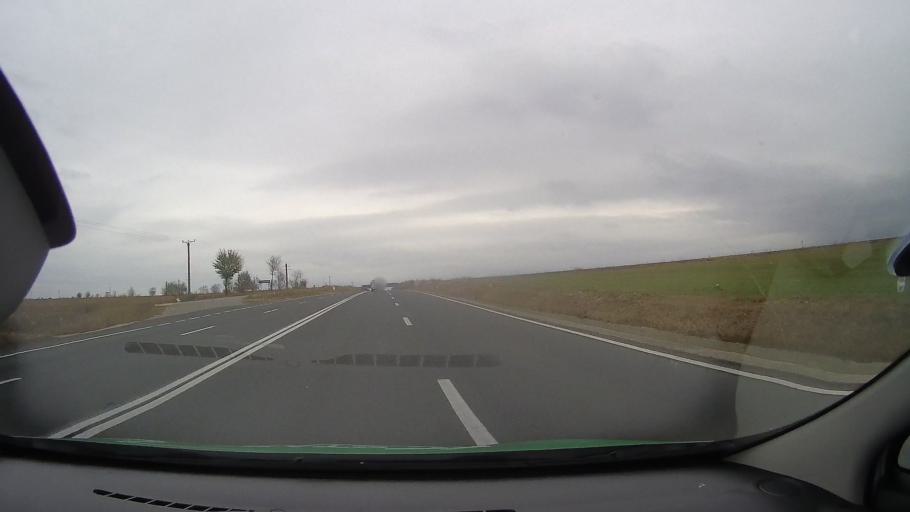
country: RO
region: Constanta
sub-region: Comuna Nicolae Balcescu
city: Nicolae Balcescu
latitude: 44.3824
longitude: 28.4016
